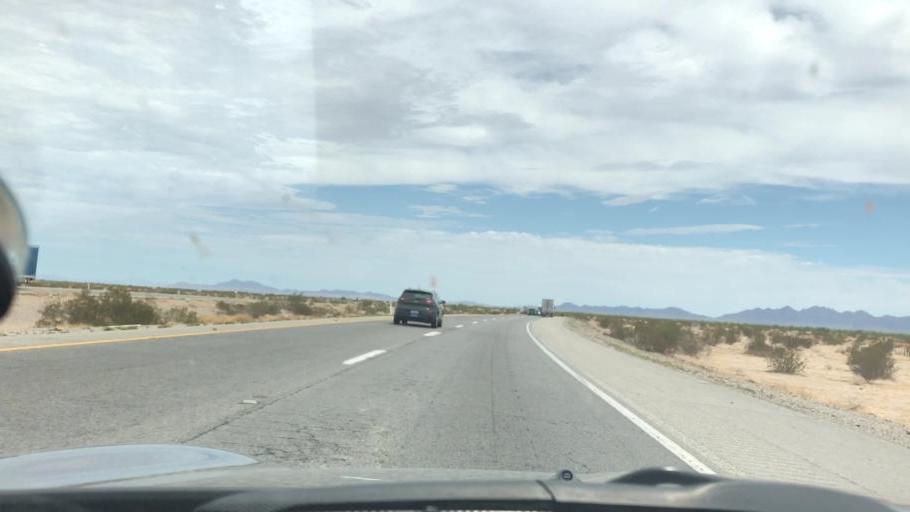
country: US
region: California
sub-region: Riverside County
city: Mesa Verde
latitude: 33.6342
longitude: -115.0797
